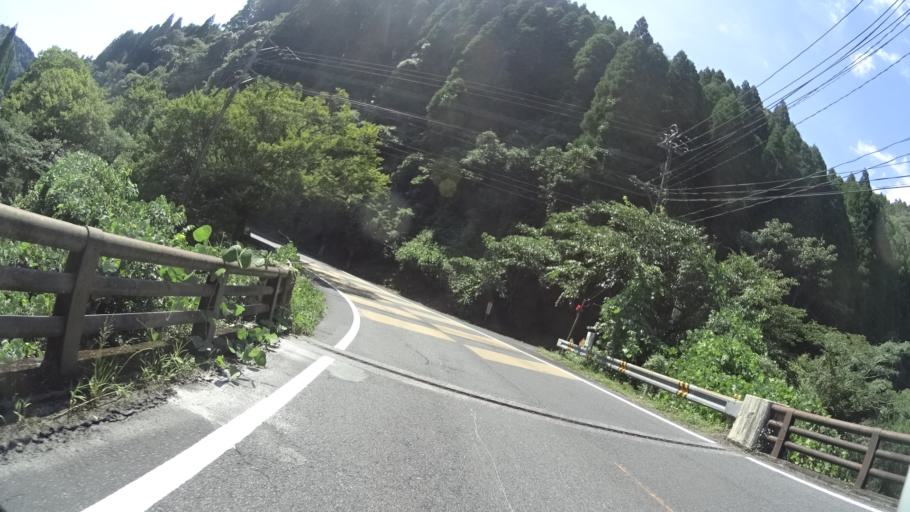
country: JP
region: Kagoshima
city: Kokubu-matsuki
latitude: 31.8342
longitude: 130.7365
